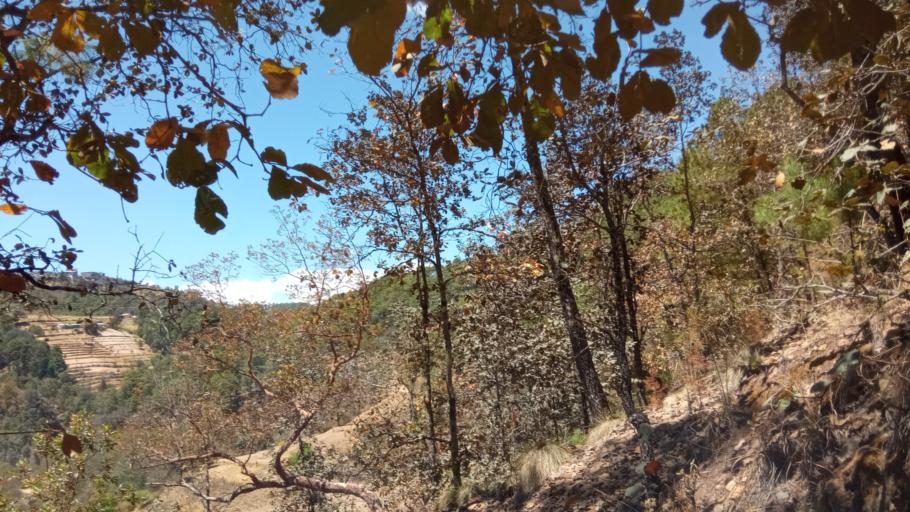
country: GT
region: San Marcos
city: Tejutla
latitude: 15.1255
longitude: -91.7919
